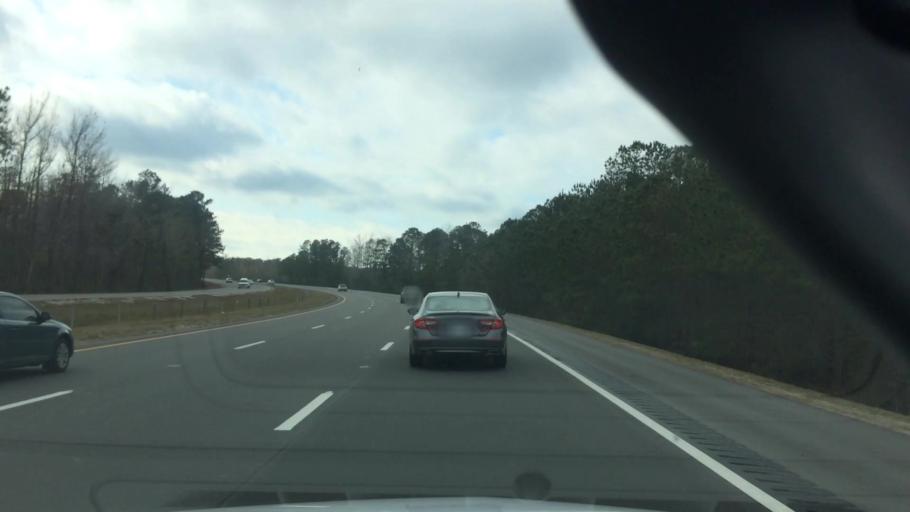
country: US
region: North Carolina
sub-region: New Hanover County
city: Skippers Corner
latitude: 34.3181
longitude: -77.8825
